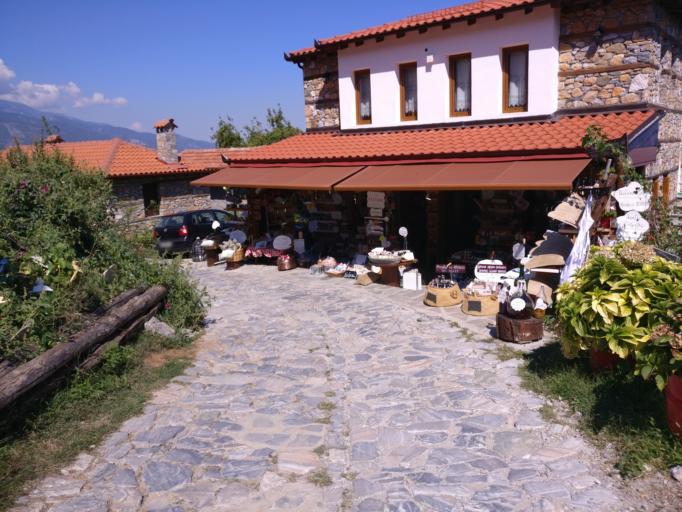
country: GR
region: Central Macedonia
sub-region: Nomos Pierias
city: Leptokarya
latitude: 39.9917
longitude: 22.5705
